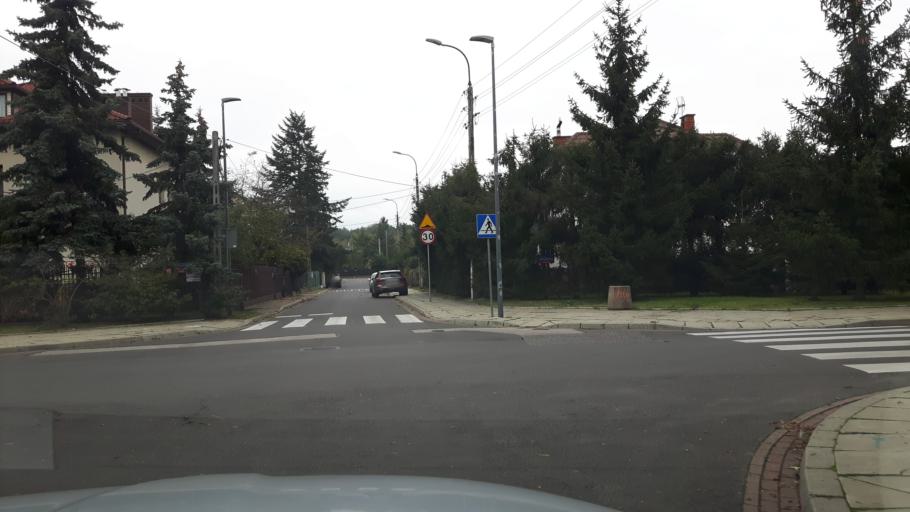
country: PL
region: Masovian Voivodeship
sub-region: Warszawa
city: Praga Poludnie
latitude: 52.2419
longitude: 21.1193
